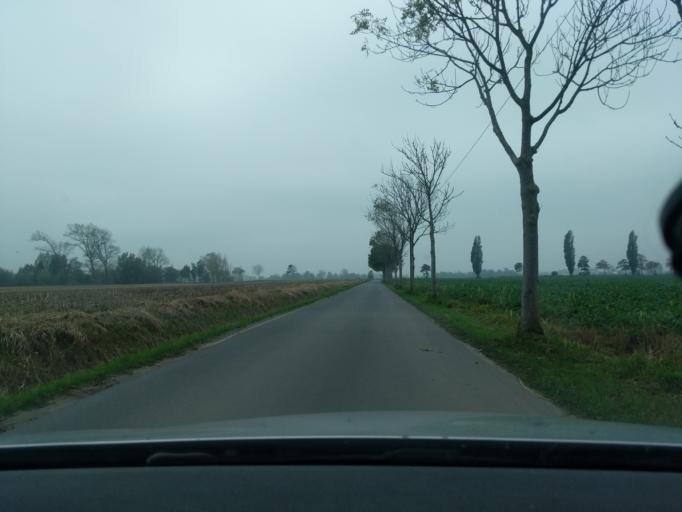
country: DE
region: Lower Saxony
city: Otterndorf
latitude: 53.8210
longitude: 8.8665
